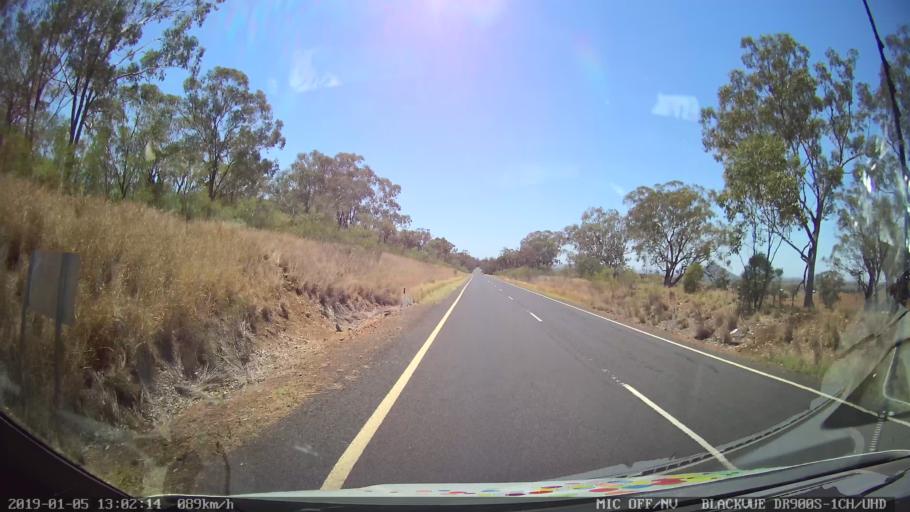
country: AU
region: New South Wales
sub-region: Narrabri
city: Boggabri
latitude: -31.1159
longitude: 149.8088
